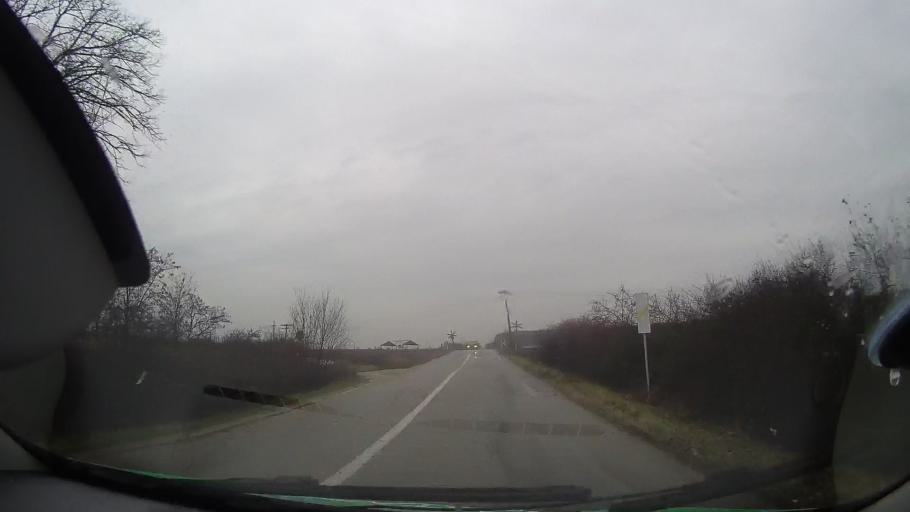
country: RO
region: Bihor
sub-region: Comuna Tinca
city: Gurbediu
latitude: 46.7723
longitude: 21.8942
